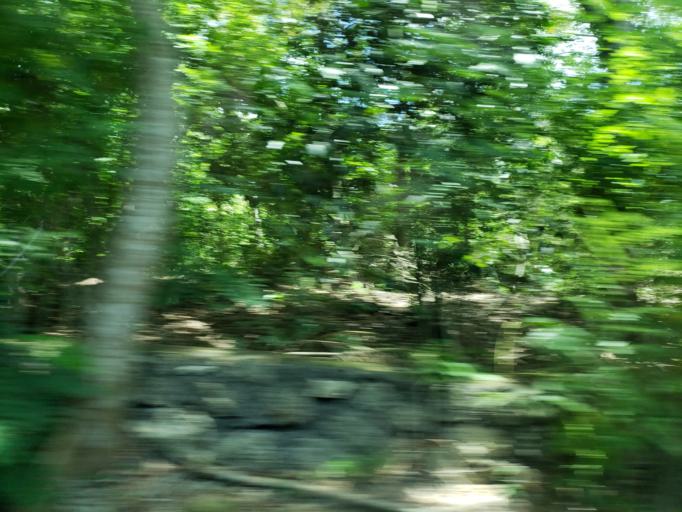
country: ID
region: Bali
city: Kangin
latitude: -8.8389
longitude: 115.1373
